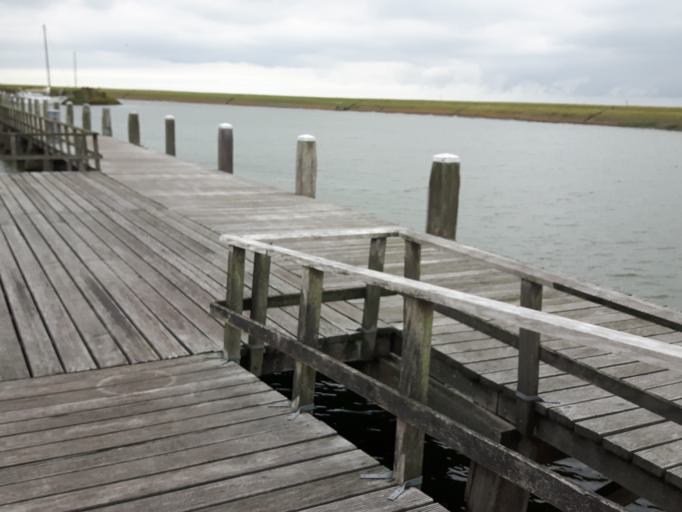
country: NL
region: Friesland
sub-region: Sudwest Fryslan
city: Koudum
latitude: 52.8867
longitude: 5.3582
